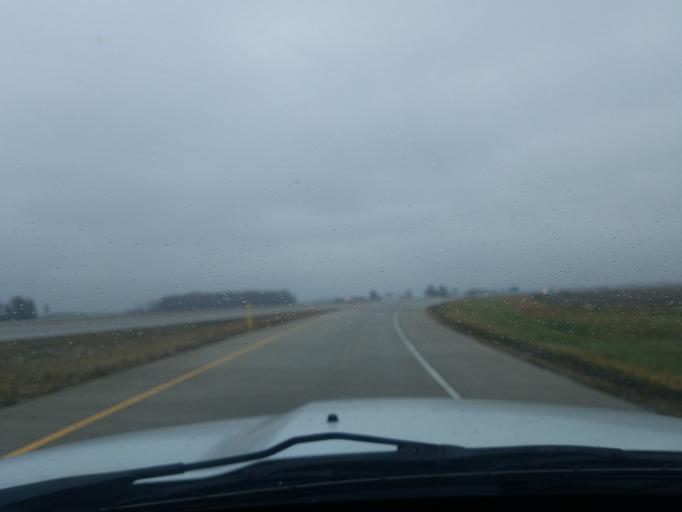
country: US
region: Indiana
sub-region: Howard County
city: Kokomo
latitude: 40.5329
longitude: -86.1101
